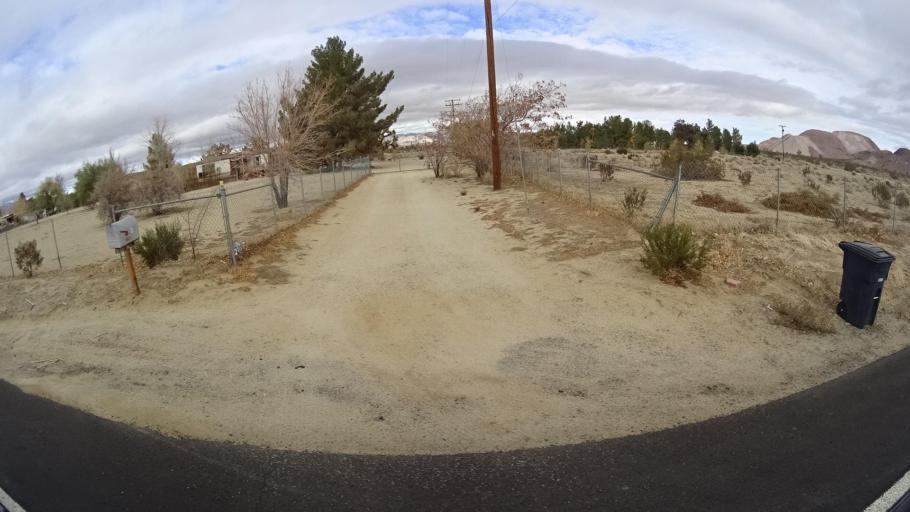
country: US
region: California
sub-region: Kern County
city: Rosamond
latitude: 34.9509
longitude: -118.2353
